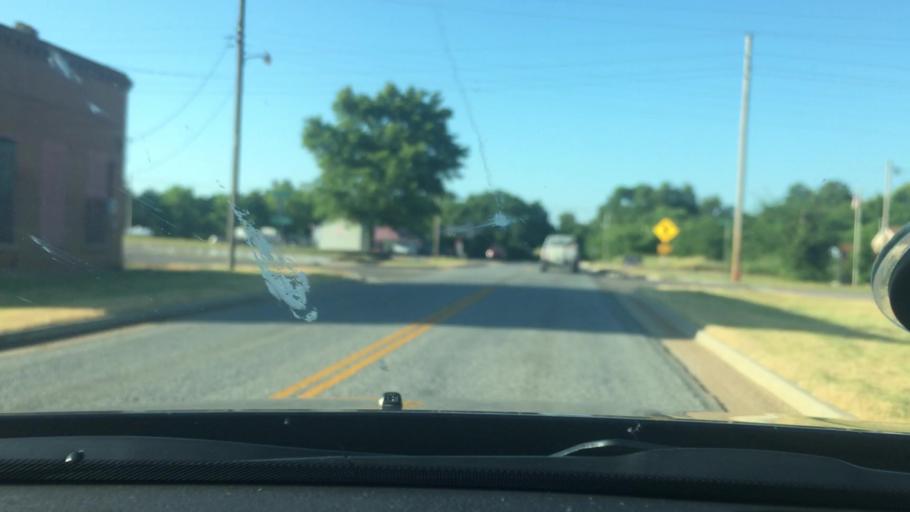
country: US
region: Oklahoma
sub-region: Murray County
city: Sulphur
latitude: 34.4046
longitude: -96.8271
